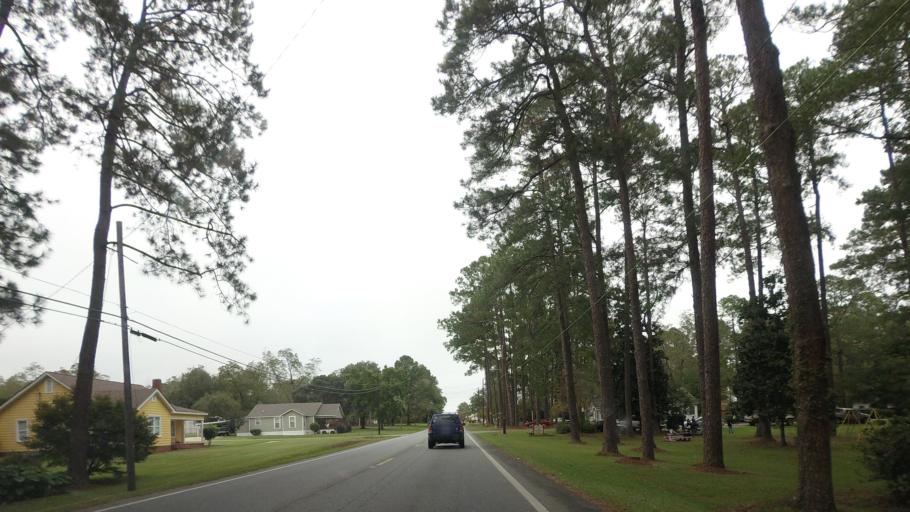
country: US
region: Georgia
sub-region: Irwin County
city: Ocilla
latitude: 31.5884
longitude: -83.2507
